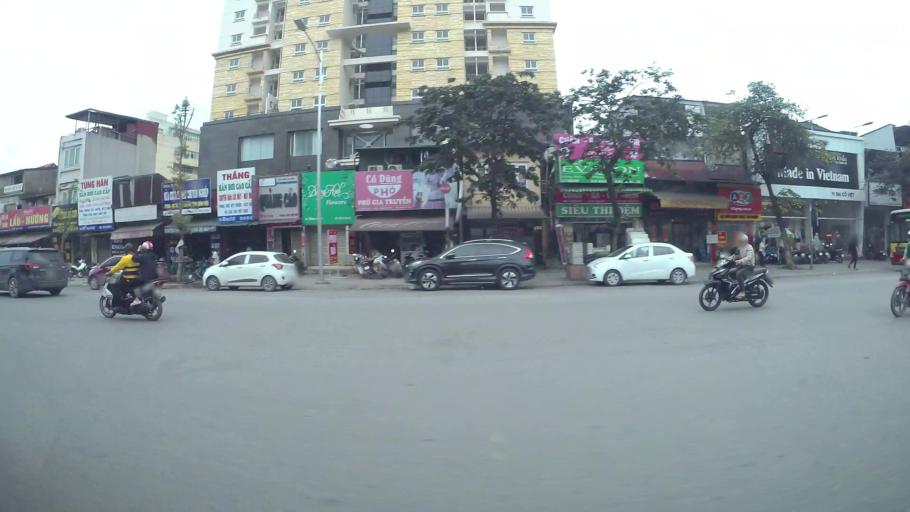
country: VN
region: Ha Noi
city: Hai BaTrung
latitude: 21.0081
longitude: 105.8470
